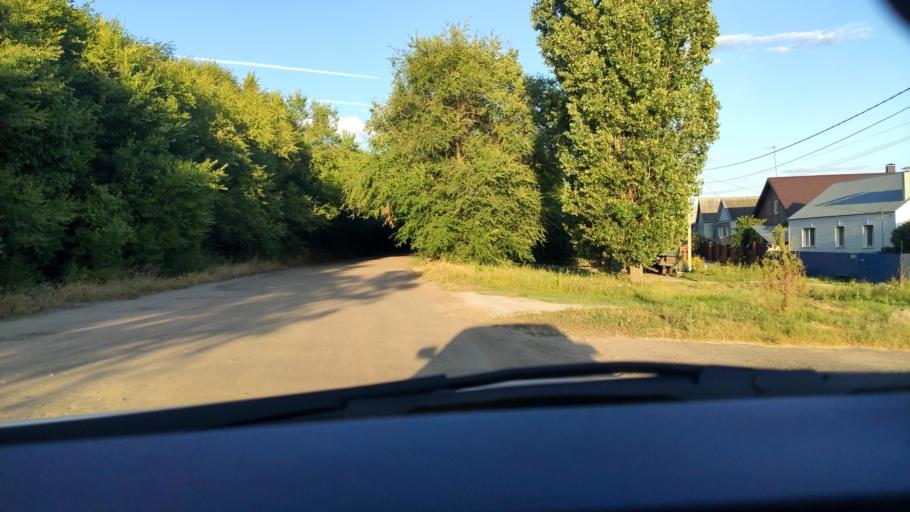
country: RU
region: Voronezj
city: Pridonskoy
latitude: 51.6848
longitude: 39.0600
